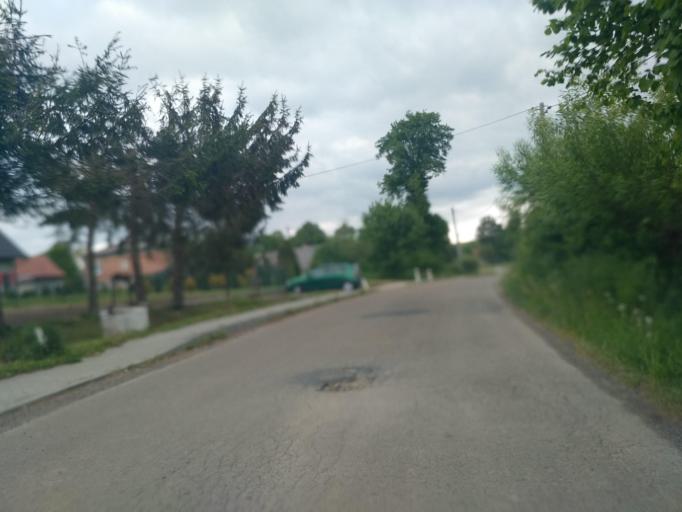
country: PL
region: Subcarpathian Voivodeship
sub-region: Powiat jasielski
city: Tarnowiec
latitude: 49.6710
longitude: 21.5738
